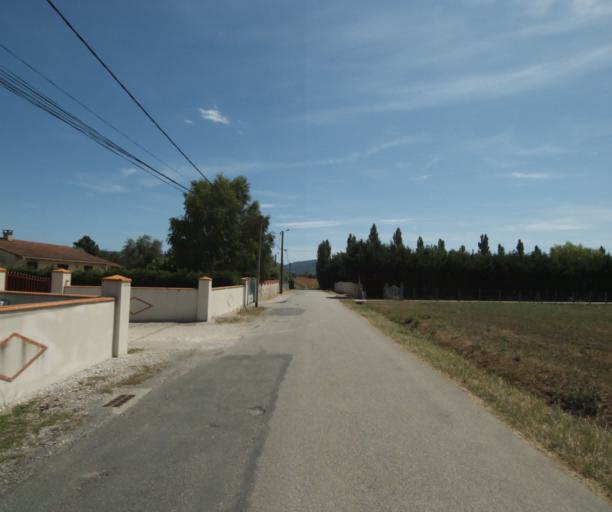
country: FR
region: Midi-Pyrenees
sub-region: Departement de la Haute-Garonne
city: Revel
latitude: 43.4889
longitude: 2.0161
